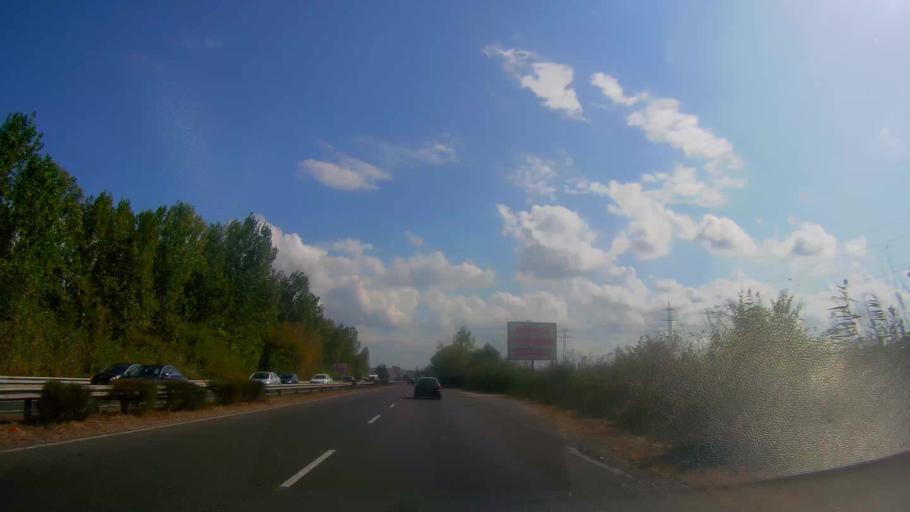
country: BG
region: Burgas
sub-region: Obshtina Burgas
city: Burgas
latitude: 42.4592
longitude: 27.4399
